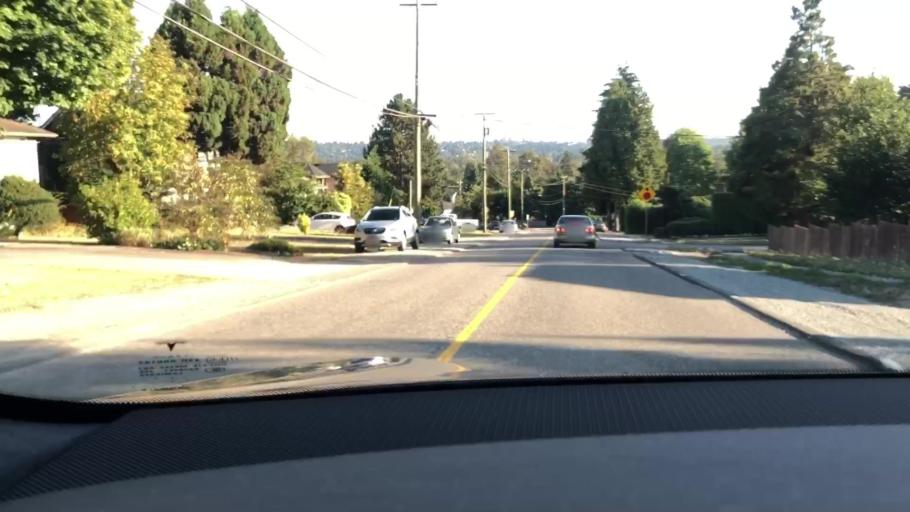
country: CA
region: British Columbia
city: Burnaby
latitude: 49.2644
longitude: -122.9702
